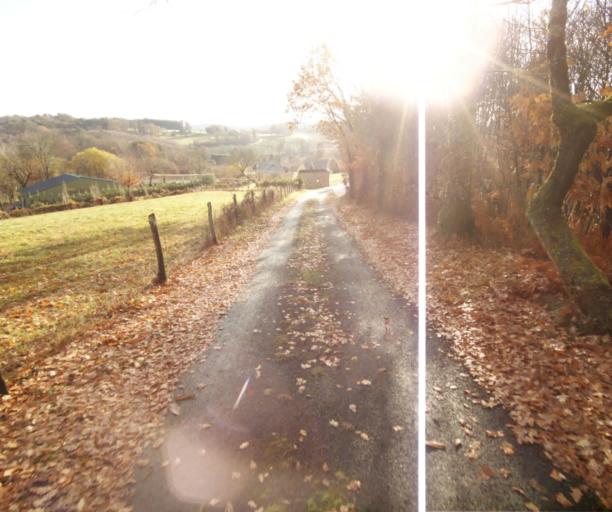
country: FR
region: Limousin
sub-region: Departement de la Correze
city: Saint-Mexant
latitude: 45.2554
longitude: 1.6371
